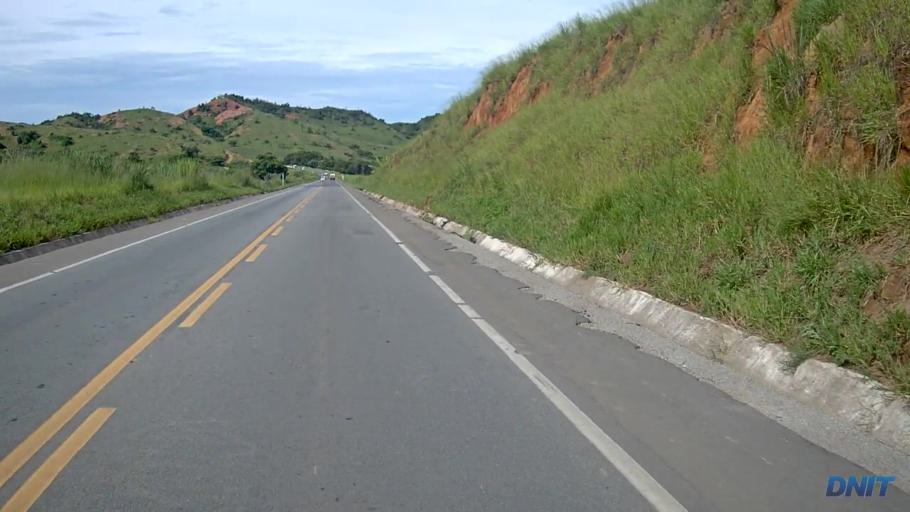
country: BR
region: Minas Gerais
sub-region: Belo Oriente
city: Belo Oriente
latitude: -19.2213
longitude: -42.3122
